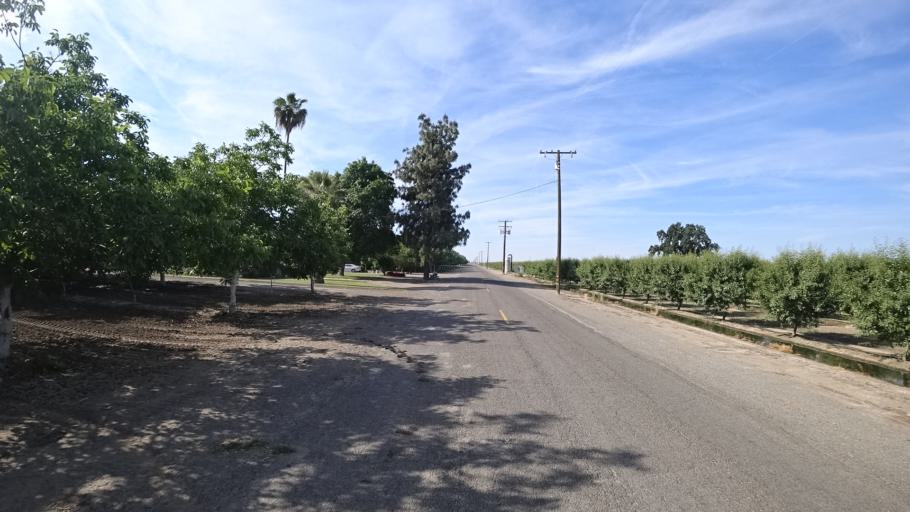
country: US
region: California
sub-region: Tulare County
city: Goshen
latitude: 36.3339
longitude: -119.4931
